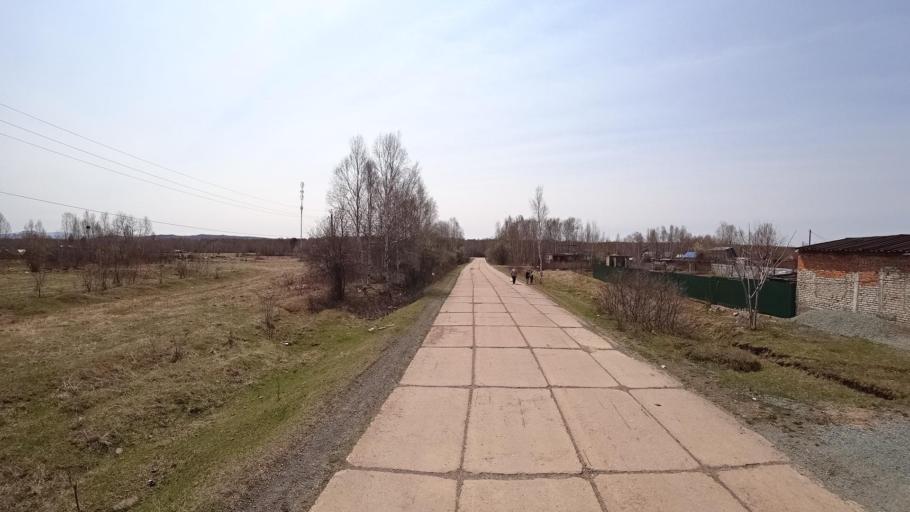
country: RU
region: Khabarovsk Krai
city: Selikhino
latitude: 50.3865
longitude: 137.3733
